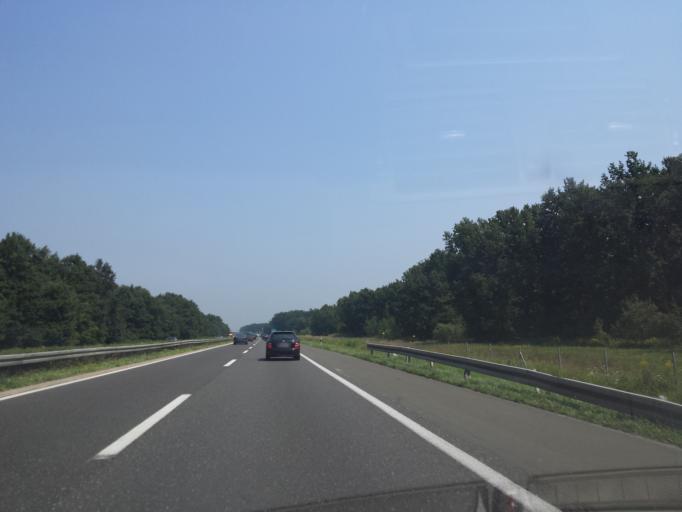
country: HR
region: Karlovacka
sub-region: Grad Karlovac
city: Karlovac
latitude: 45.5484
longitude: 15.5966
